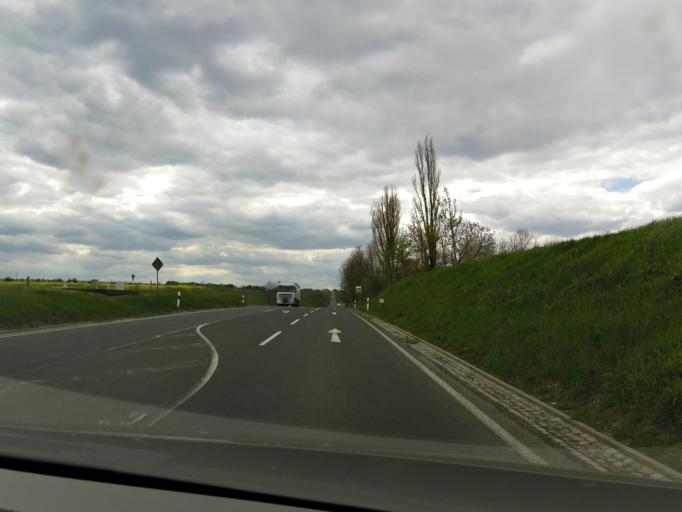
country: DE
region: Thuringia
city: Rannstedt
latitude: 51.1026
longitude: 11.5487
